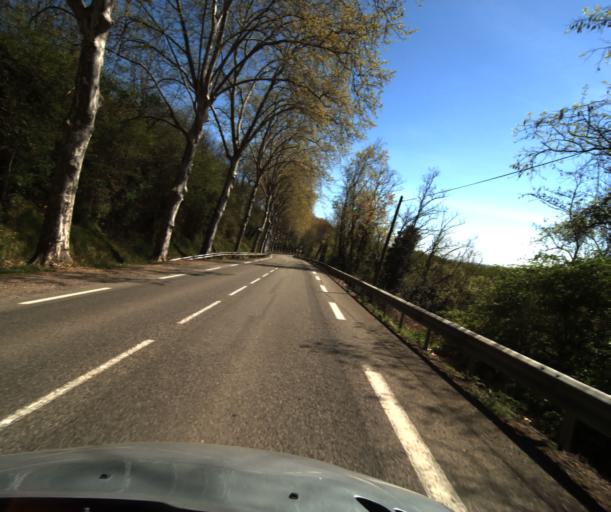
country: FR
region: Midi-Pyrenees
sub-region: Departement du Tarn-et-Garonne
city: Lafrancaise
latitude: 44.1224
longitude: 1.2422
